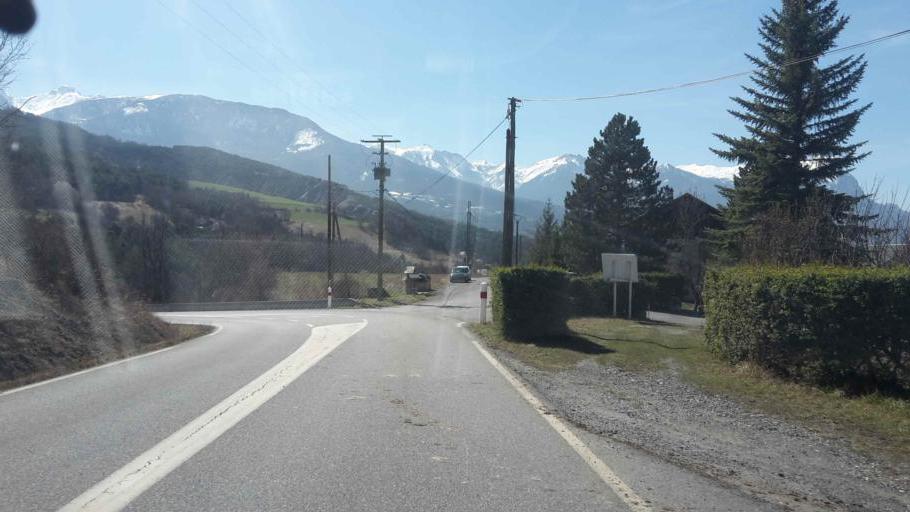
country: FR
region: Provence-Alpes-Cote d'Azur
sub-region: Departement des Hautes-Alpes
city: Embrun
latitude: 44.5676
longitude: 6.5214
